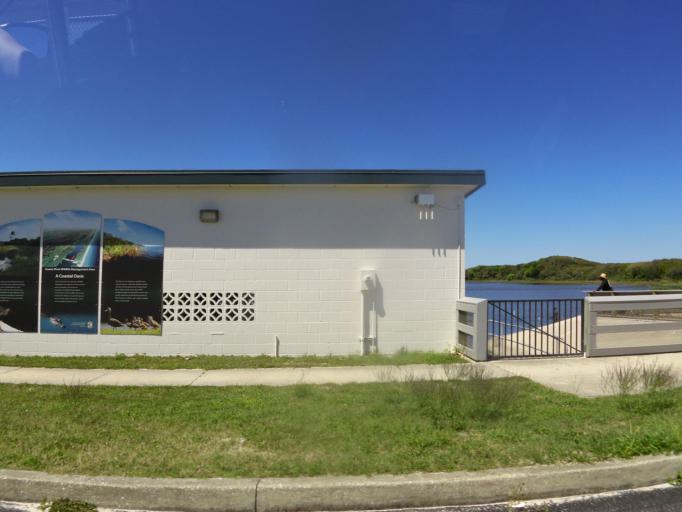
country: US
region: Florida
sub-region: Saint Johns County
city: Villano Beach
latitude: 30.0233
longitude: -81.3285
